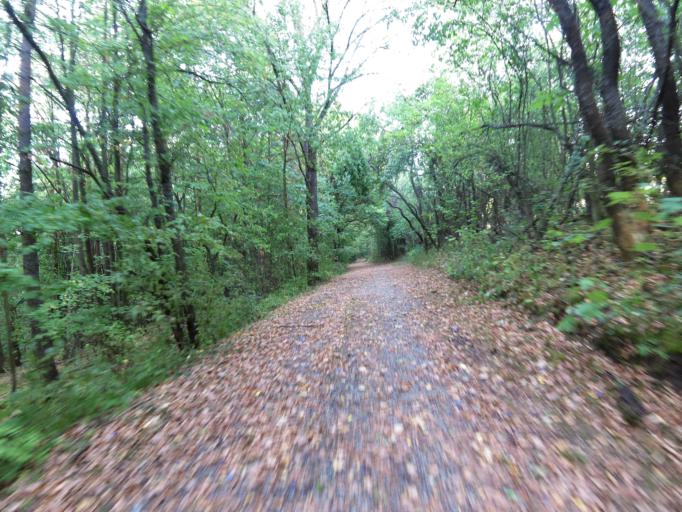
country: DE
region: Bavaria
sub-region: Regierungsbezirk Unterfranken
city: Zell am Main
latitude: 49.8058
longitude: 9.8698
